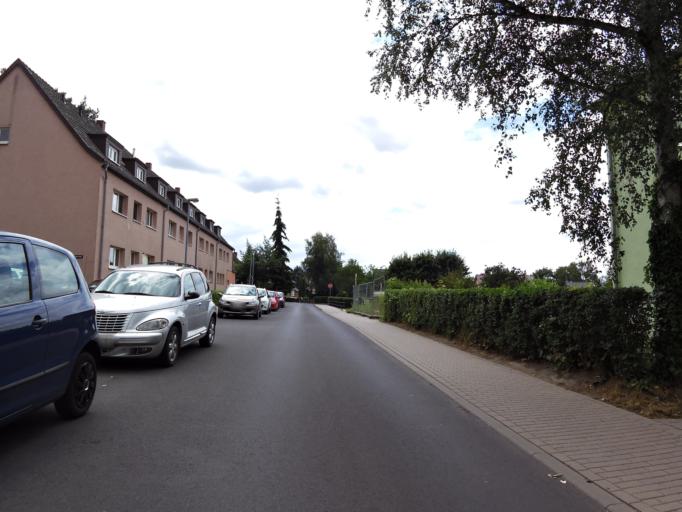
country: DE
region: Thuringia
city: Bad Salzungen
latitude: 50.8101
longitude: 10.2435
